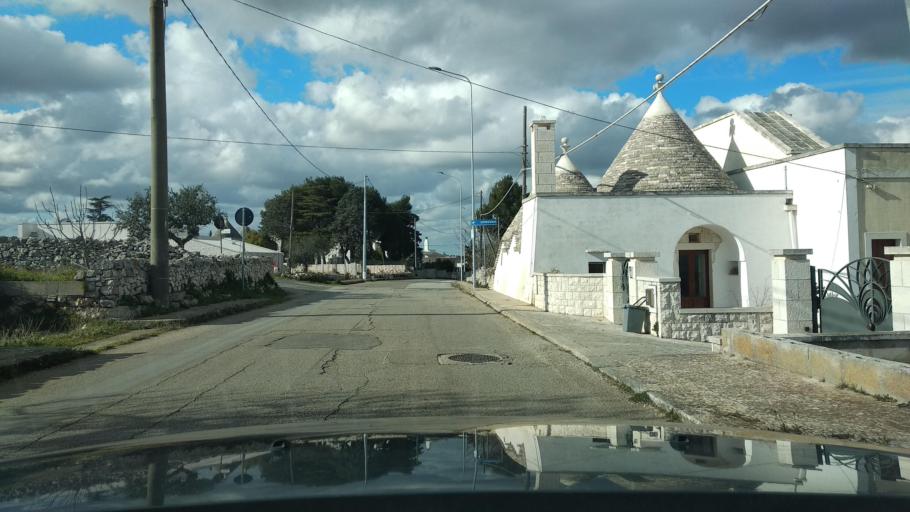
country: IT
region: Apulia
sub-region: Provincia di Brindisi
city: Cisternino
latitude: 40.7456
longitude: 17.4168
